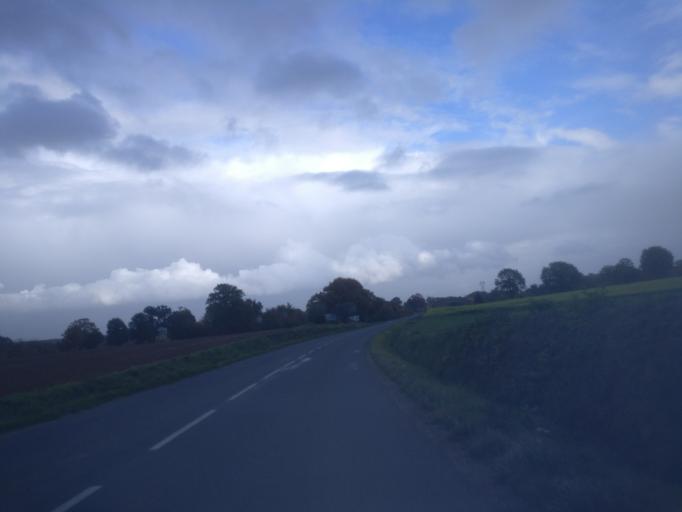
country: FR
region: Brittany
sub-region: Departement d'Ille-et-Vilaine
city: Goven
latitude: 48.0352
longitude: -1.8215
